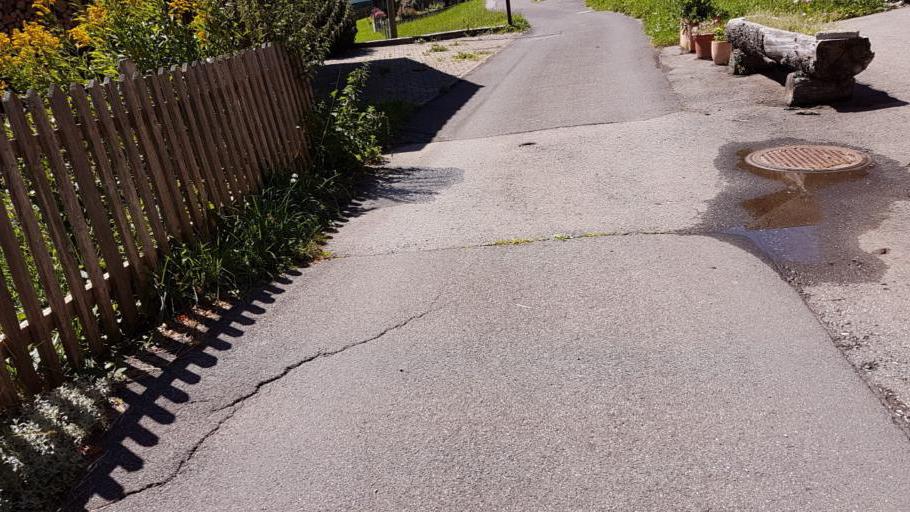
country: CH
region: Bern
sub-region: Frutigen-Niedersimmental District
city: Adelboden
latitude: 46.4850
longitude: 7.5561
